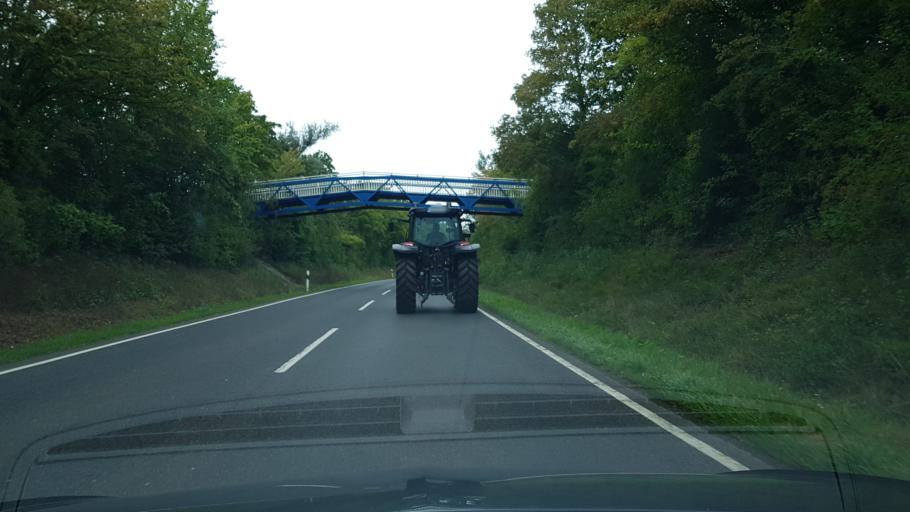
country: DE
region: North Rhine-Westphalia
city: Meckenheim
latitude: 50.6225
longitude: 7.0340
